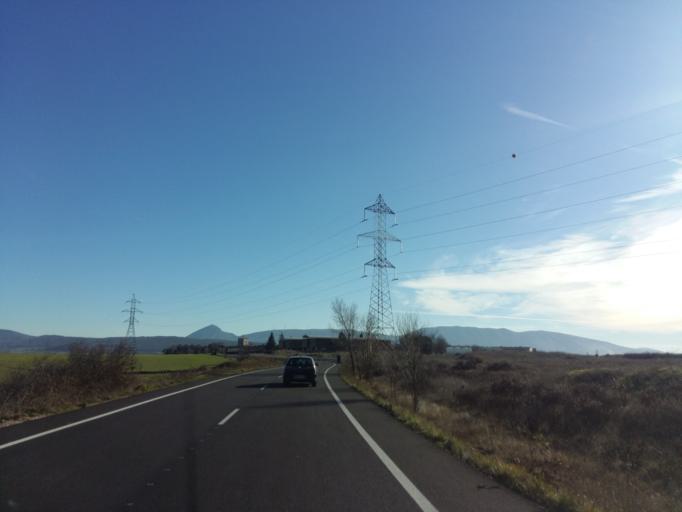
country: ES
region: Navarre
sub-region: Provincia de Navarra
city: Iturrama
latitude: 42.7928
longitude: -1.6505
